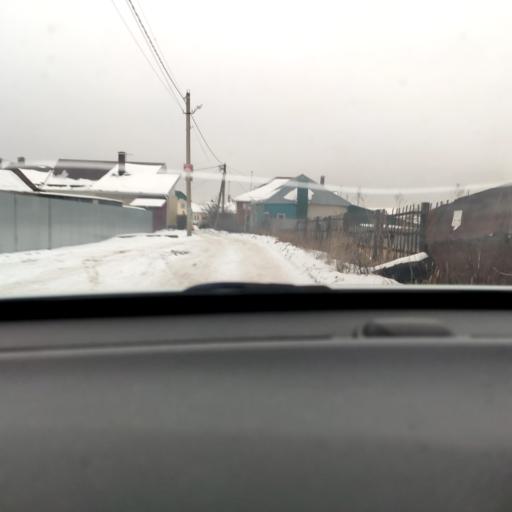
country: RU
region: Voronezj
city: Somovo
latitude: 51.7512
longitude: 39.3414
